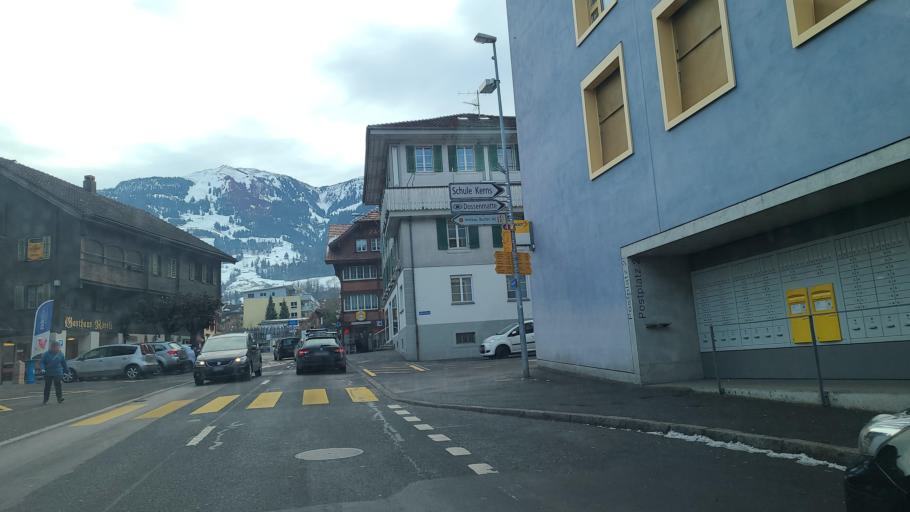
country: CH
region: Obwalden
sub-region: Obwalden
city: Kerns
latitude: 46.9009
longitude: 8.2745
